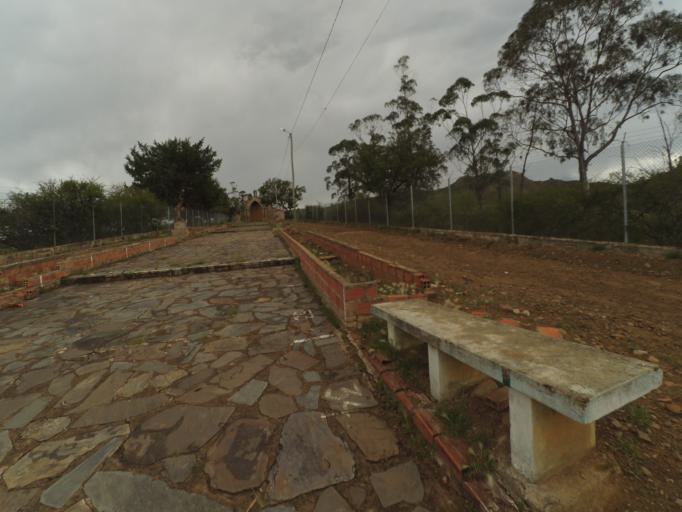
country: BO
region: Chuquisaca
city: Padilla
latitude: -19.3153
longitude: -64.3088
